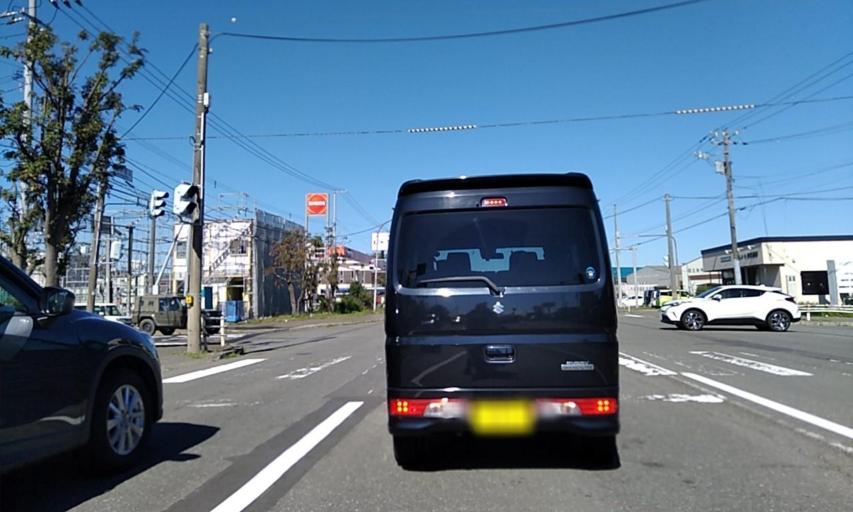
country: JP
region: Hokkaido
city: Kitahiroshima
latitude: 42.8938
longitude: 141.5670
